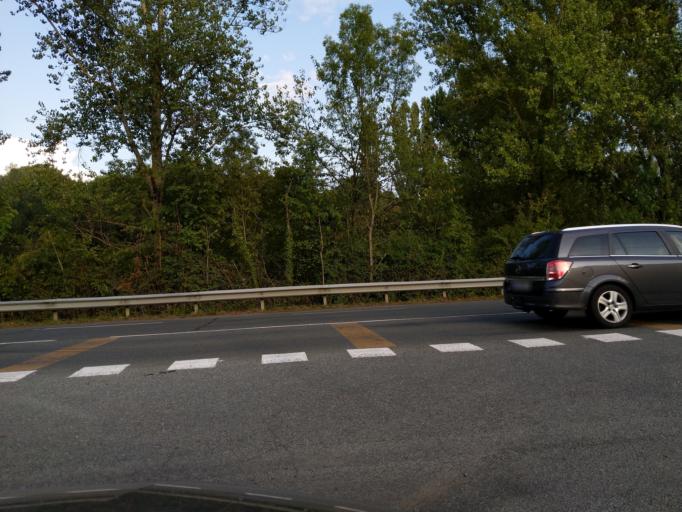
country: FR
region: Midi-Pyrenees
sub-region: Departement du Tarn
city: Realmont
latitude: 43.7832
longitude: 2.1867
